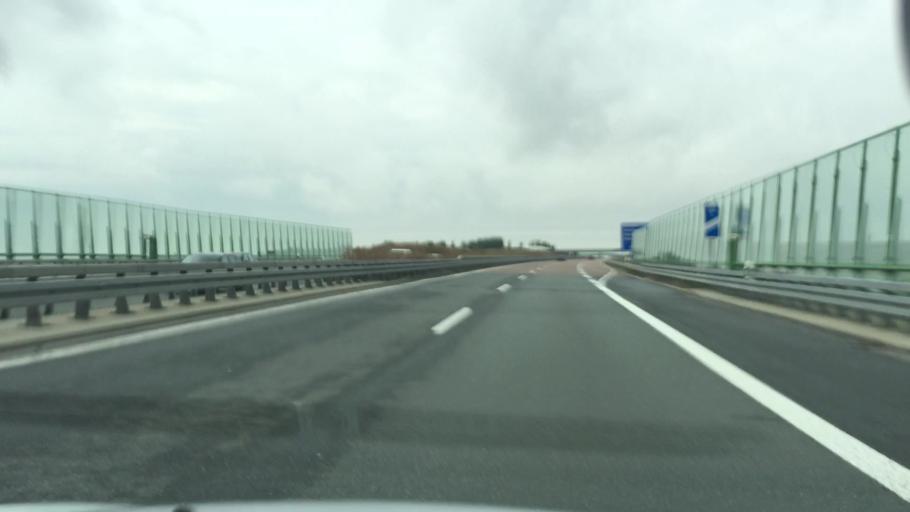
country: DE
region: Saxony
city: Narsdorf
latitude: 50.9905
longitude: 12.6928
